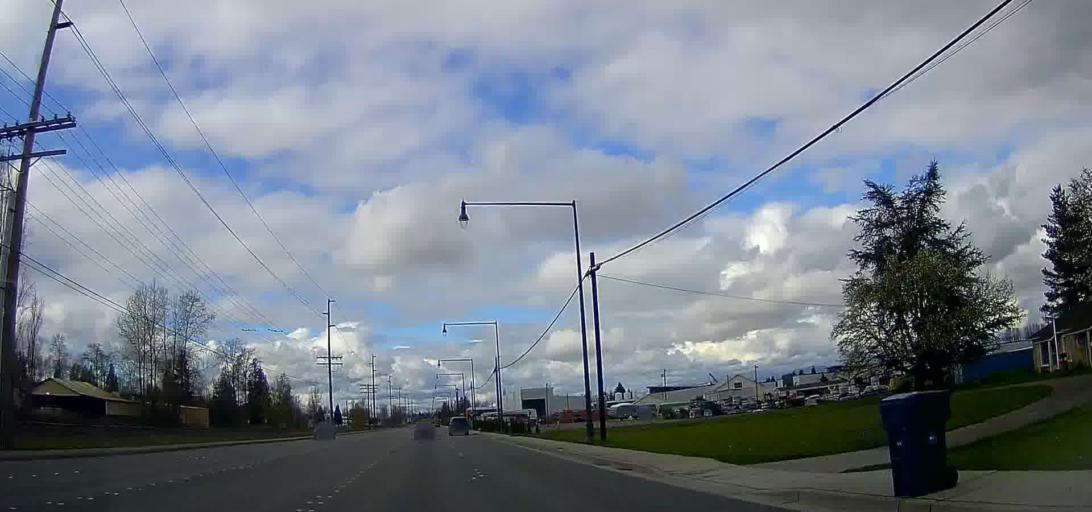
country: US
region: Washington
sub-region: Snohomish County
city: Smokey Point
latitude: 48.1130
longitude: -122.1799
